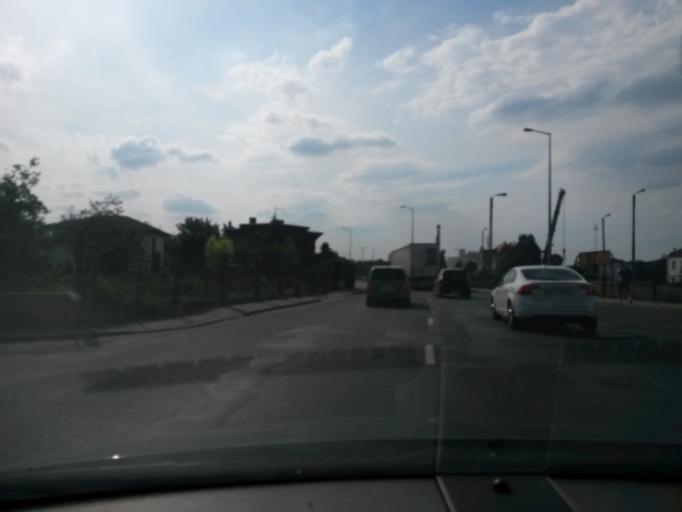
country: PL
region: Greater Poland Voivodeship
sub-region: Powiat gostynski
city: Gostyn
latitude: 51.8834
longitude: 17.0093
